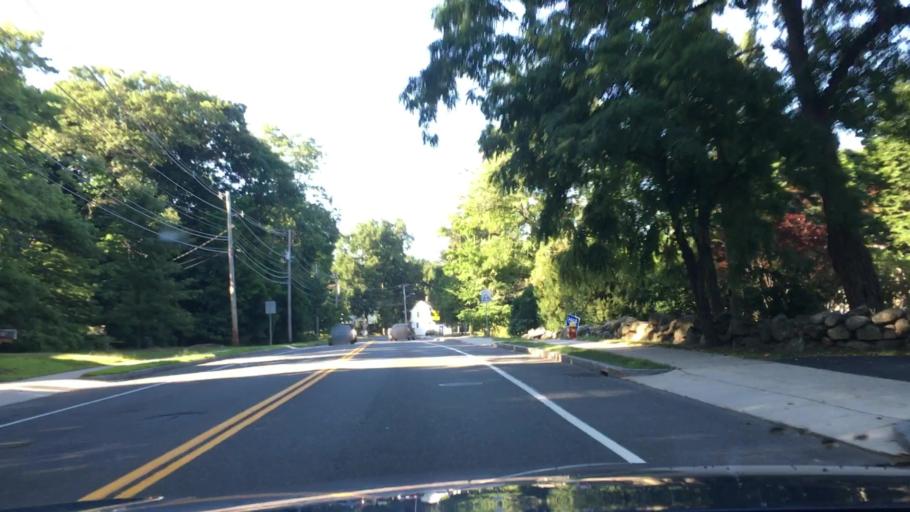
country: US
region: Massachusetts
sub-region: Middlesex County
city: Billerica
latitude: 42.5521
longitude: -71.2725
